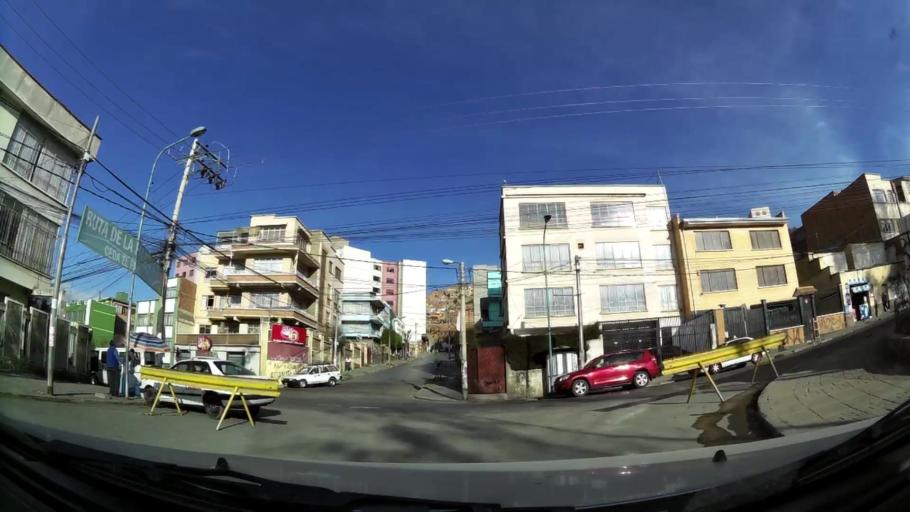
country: BO
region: La Paz
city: La Paz
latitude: -16.4851
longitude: -68.1224
